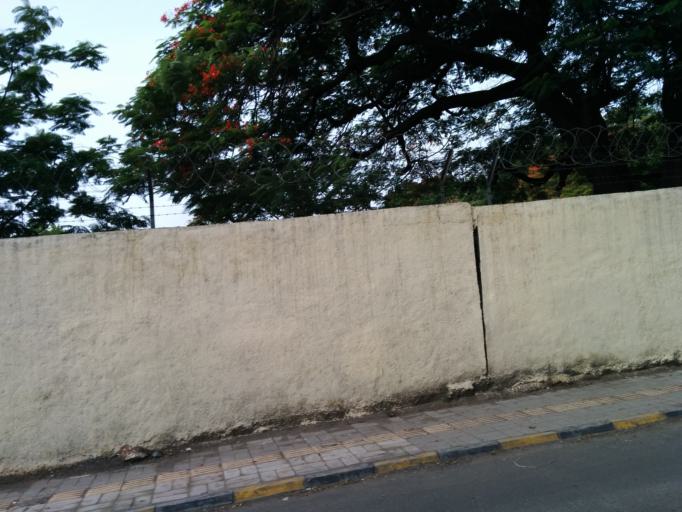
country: IN
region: Maharashtra
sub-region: Pune Division
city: Pune
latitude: 18.5063
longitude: 73.9088
